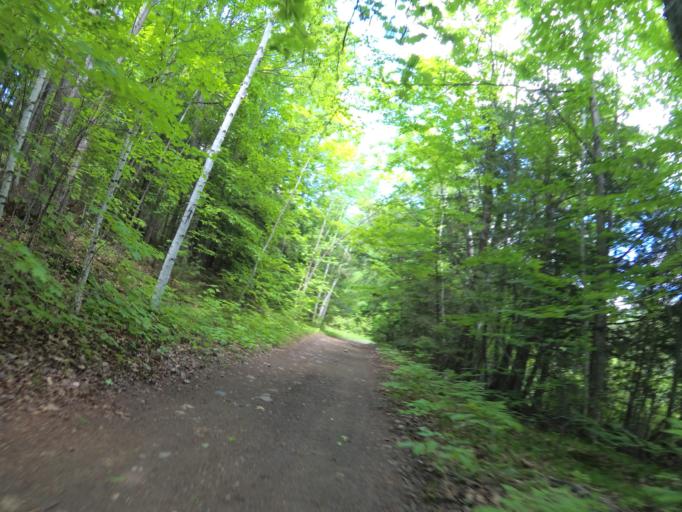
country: CA
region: Ontario
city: Renfrew
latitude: 45.0526
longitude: -76.8407
